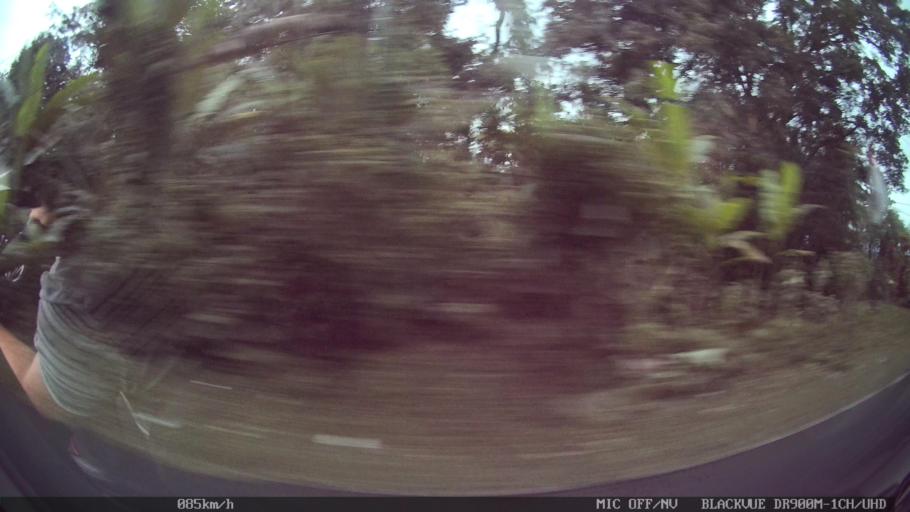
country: ID
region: Bali
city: Penebel
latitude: -8.4093
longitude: 115.1456
